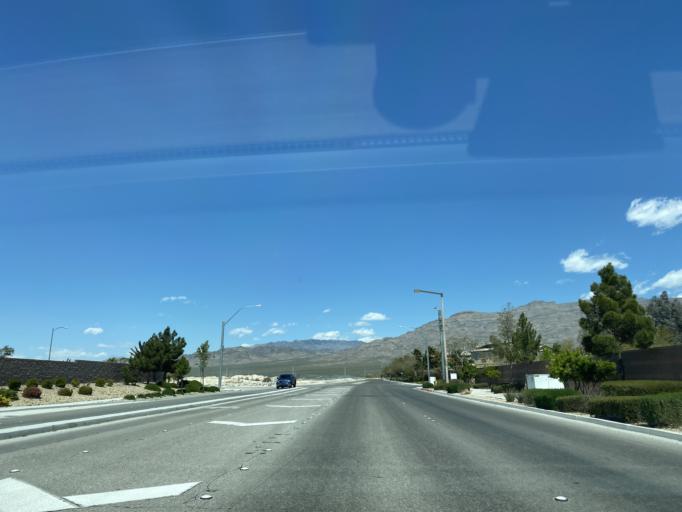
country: US
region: Nevada
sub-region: Clark County
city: North Las Vegas
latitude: 36.3194
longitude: -115.2246
